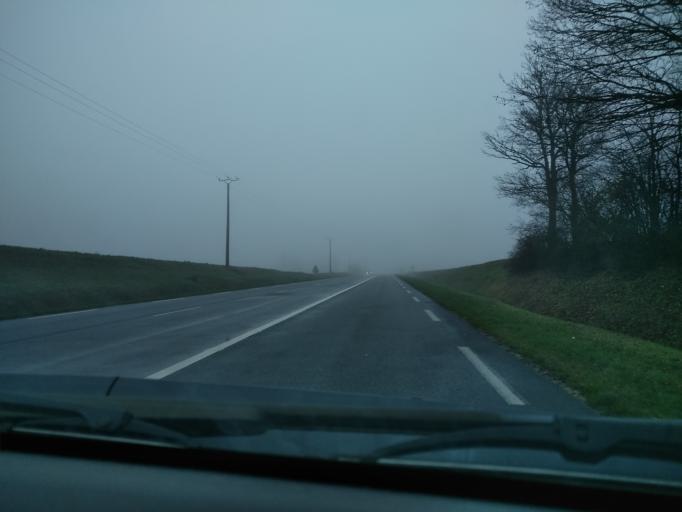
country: FR
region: Centre
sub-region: Departement d'Eure-et-Loir
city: Marboue
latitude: 48.1426
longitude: 1.3472
